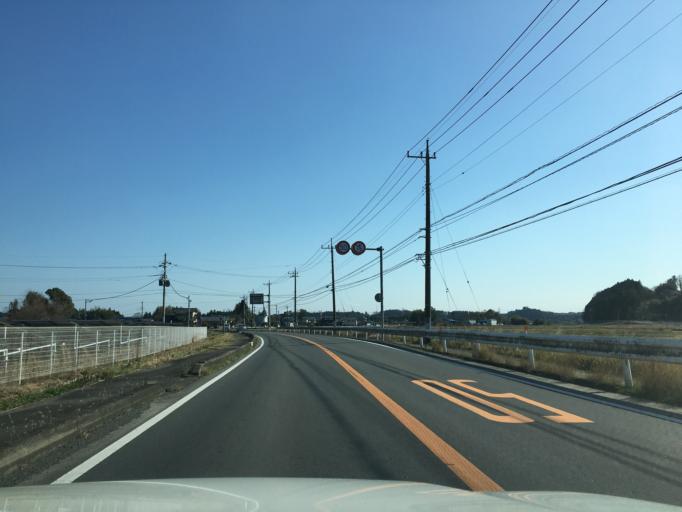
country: JP
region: Ibaraki
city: Omiya
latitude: 36.5082
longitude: 140.3713
